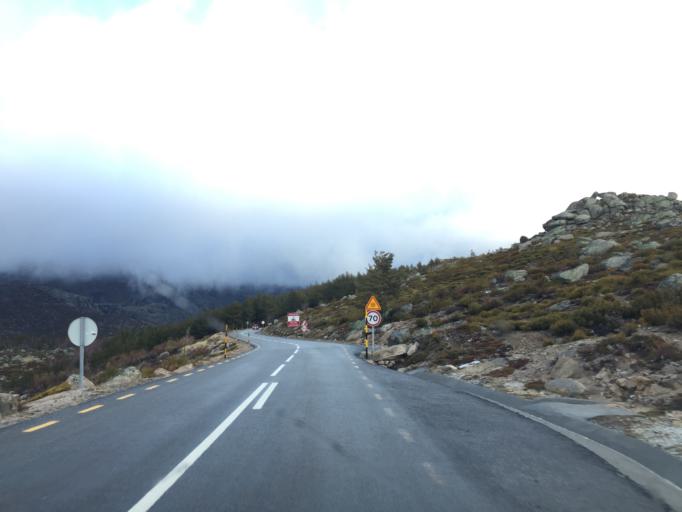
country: PT
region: Castelo Branco
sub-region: Covilha
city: Covilha
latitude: 40.3175
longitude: -7.5745
